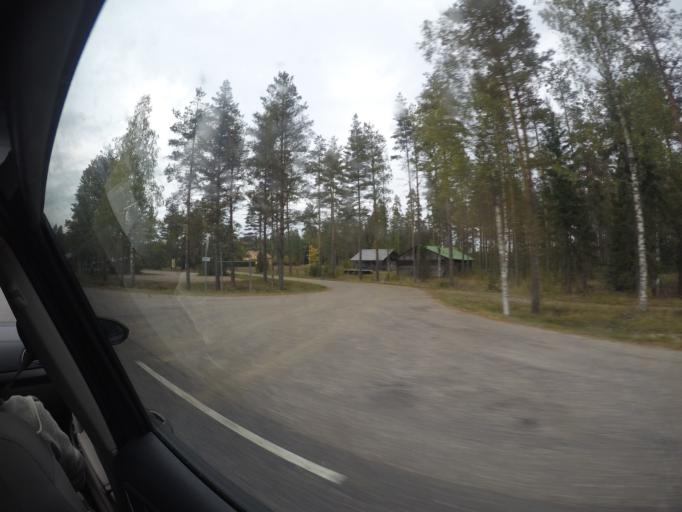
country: FI
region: Pirkanmaa
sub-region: Ylae-Pirkanmaa
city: Juupajoki
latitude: 61.8330
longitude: 24.2835
